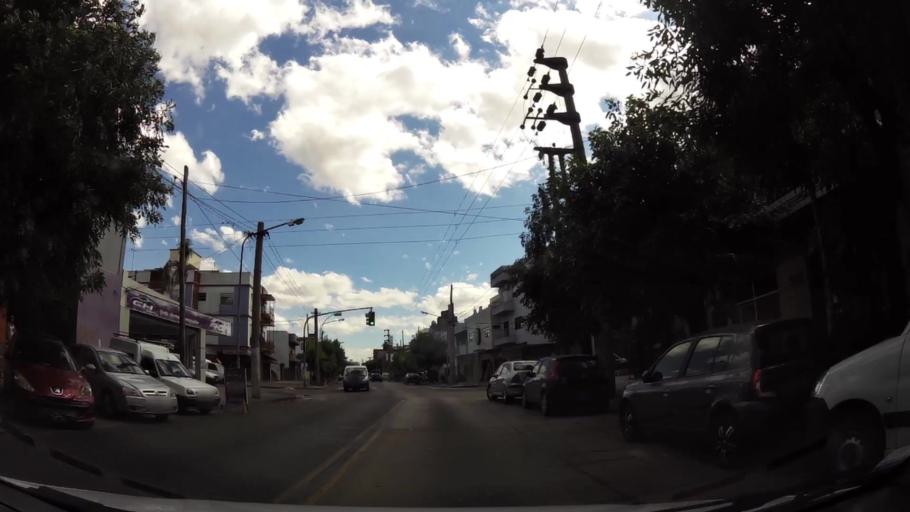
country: AR
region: Buenos Aires
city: San Justo
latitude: -34.6581
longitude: -58.5416
